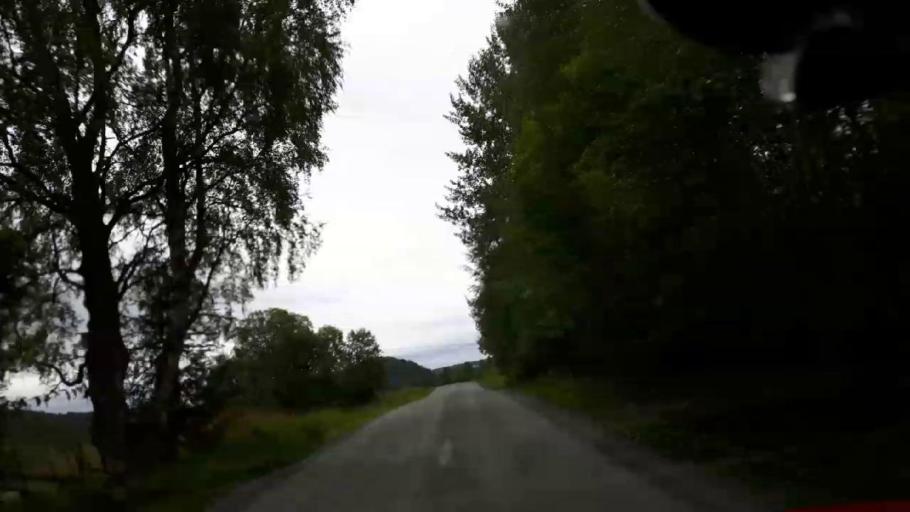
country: SE
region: Jaemtland
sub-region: Braecke Kommun
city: Braecke
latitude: 63.0820
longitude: 15.2800
